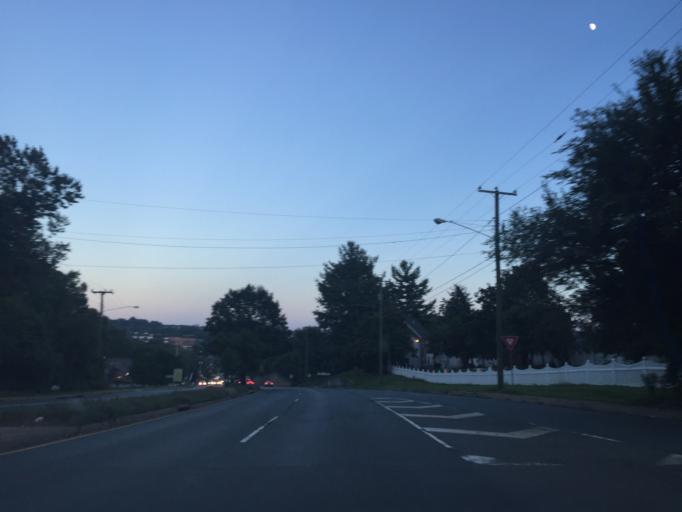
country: US
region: Virginia
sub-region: City of Charlottesville
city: Charlottesville
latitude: 38.0371
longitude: -78.4643
